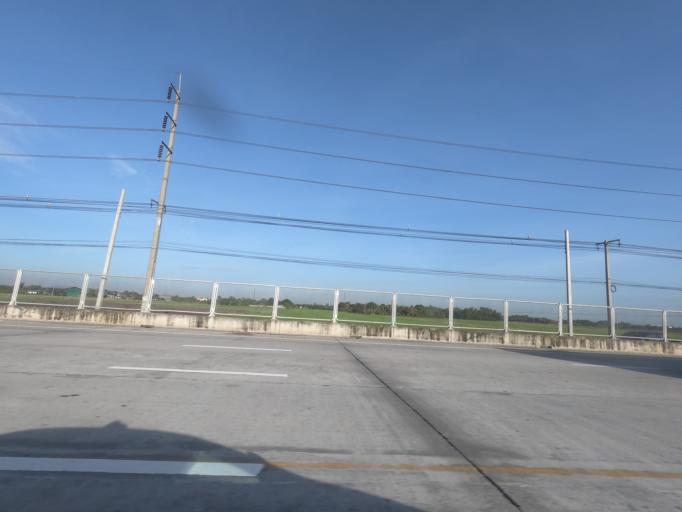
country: TH
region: Pathum Thani
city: Lam Luk Ka
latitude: 13.9599
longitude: 100.7127
